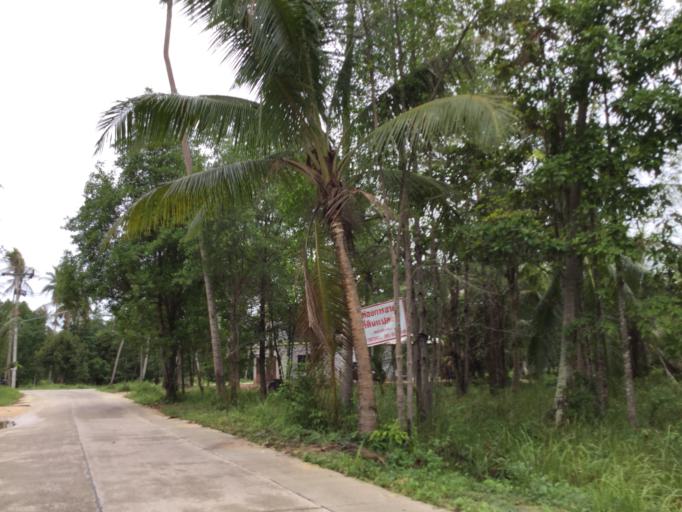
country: TH
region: Surat Thani
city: Ko Pha-Ngan
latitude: 9.7223
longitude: 100.0066
